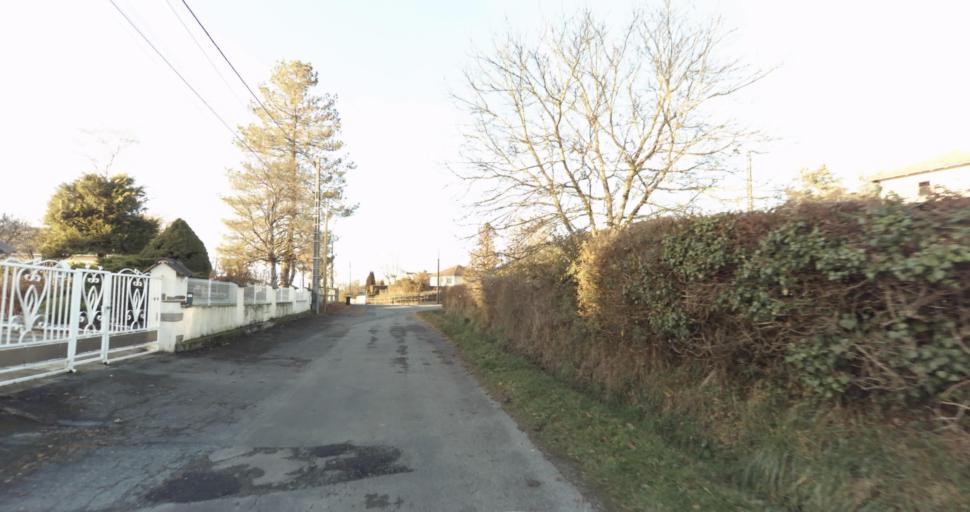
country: FR
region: Limousin
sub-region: Departement de la Haute-Vienne
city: Aixe-sur-Vienne
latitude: 45.7909
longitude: 1.1473
